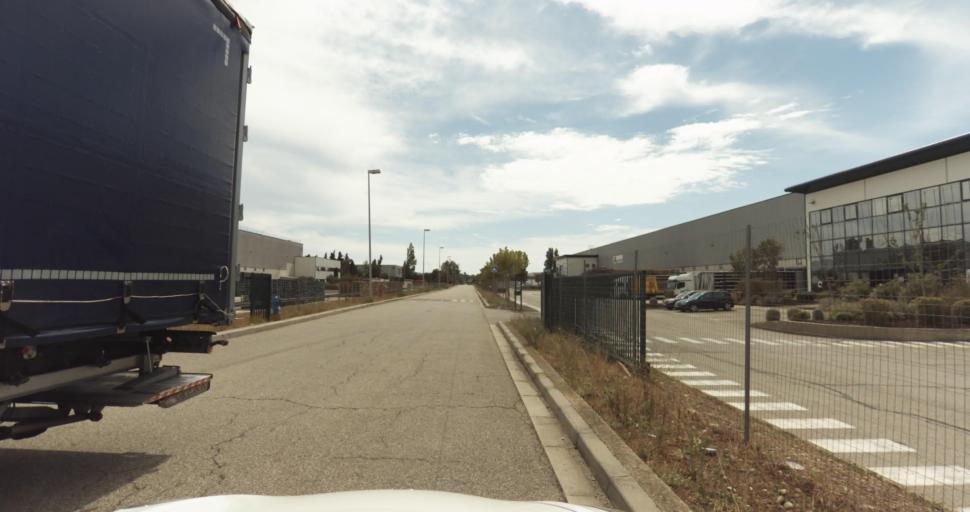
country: FR
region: Provence-Alpes-Cote d'Azur
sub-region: Departement des Bouches-du-Rhone
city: Miramas
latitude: 43.6082
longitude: 4.9981
